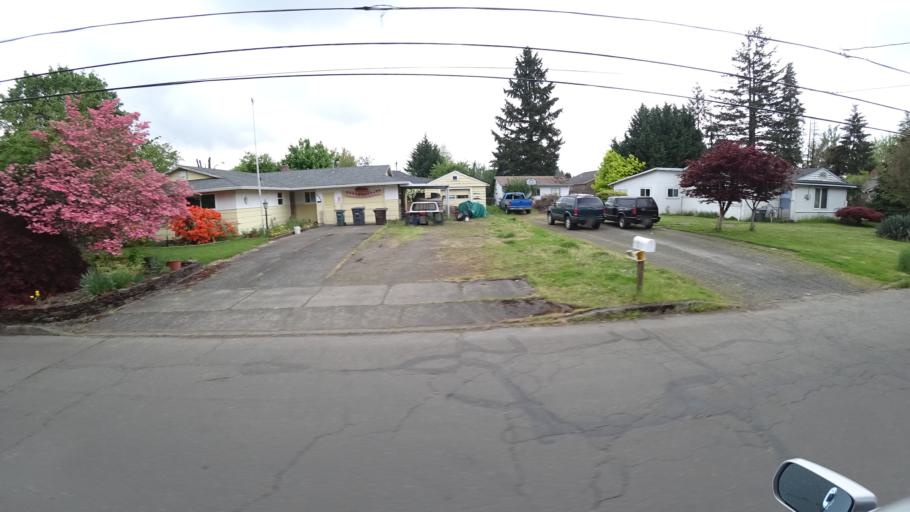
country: US
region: Oregon
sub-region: Washington County
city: Hillsboro
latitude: 45.5360
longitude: -122.9702
